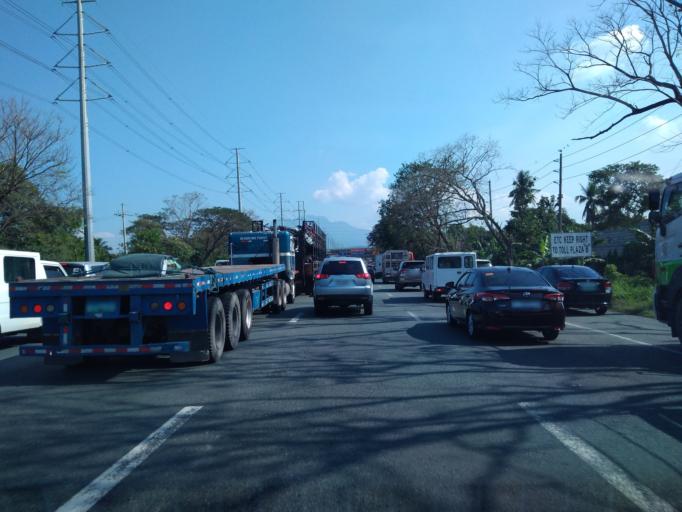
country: PH
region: Calabarzon
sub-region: Province of Laguna
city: Prinza
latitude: 14.2233
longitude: 121.1226
